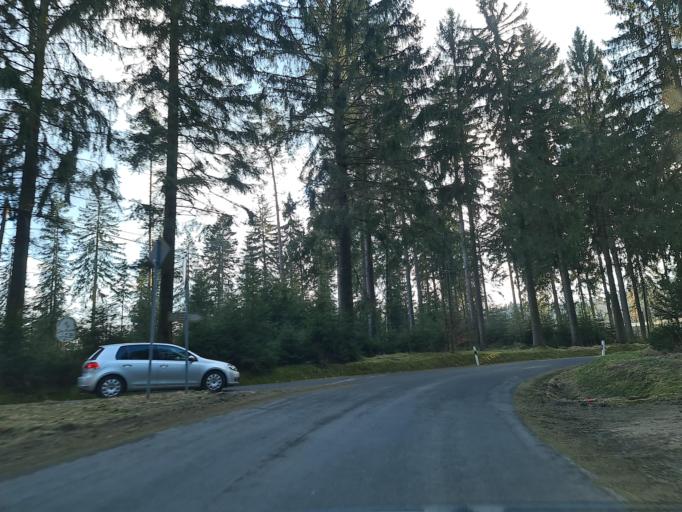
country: DE
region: Saxony
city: Muldenhammer
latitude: 50.4925
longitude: 12.4568
